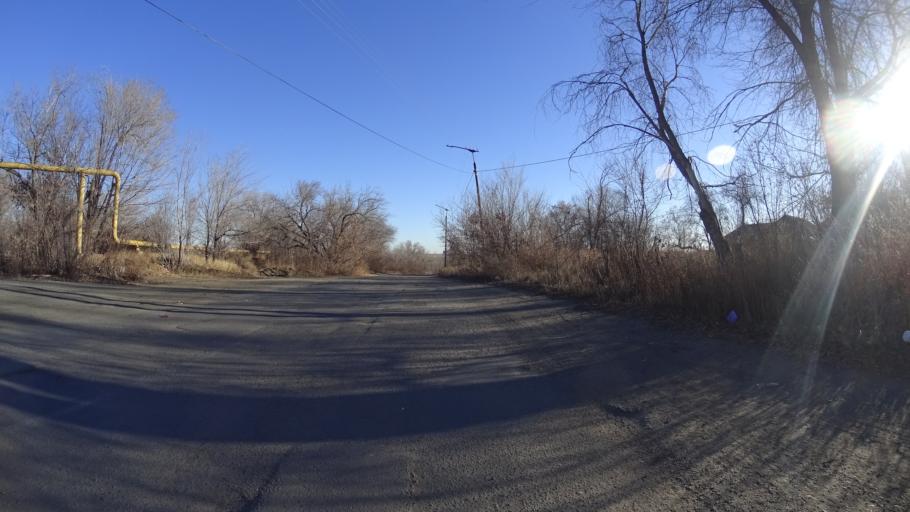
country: RU
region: Chelyabinsk
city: Troitsk
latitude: 54.1008
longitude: 61.5550
